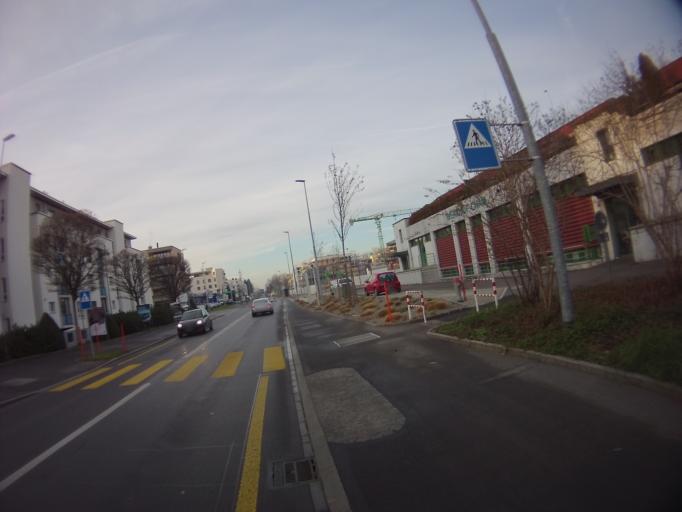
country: CH
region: Zug
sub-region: Zug
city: Cham
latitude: 47.1846
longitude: 8.4561
